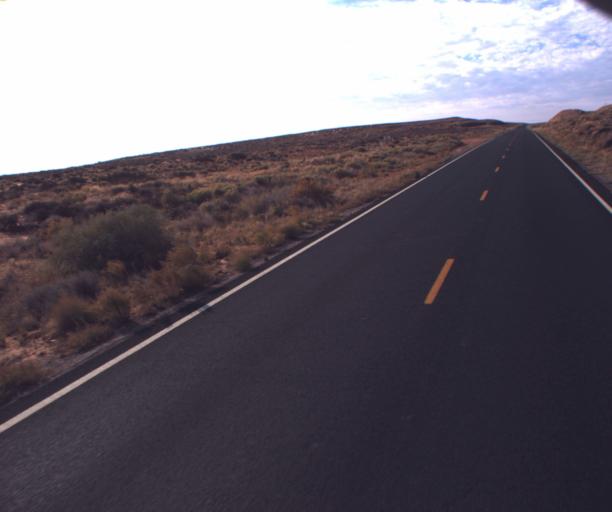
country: US
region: Arizona
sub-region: Apache County
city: Many Farms
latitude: 36.8910
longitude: -109.6269
